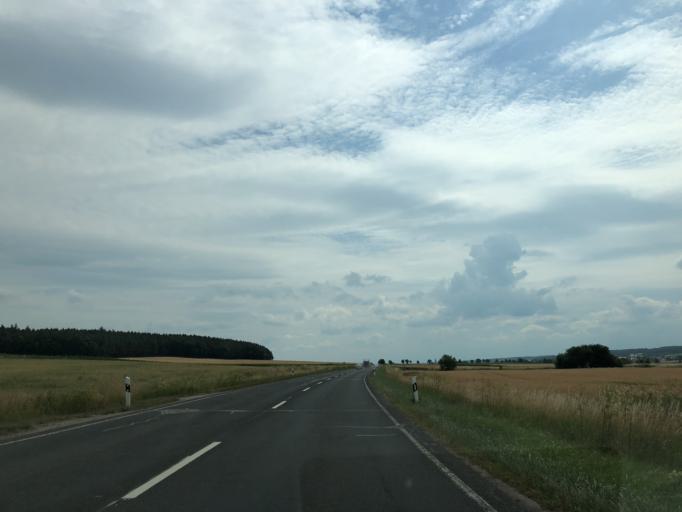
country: DE
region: Bavaria
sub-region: Regierungsbezirk Mittelfranken
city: Wachenroth
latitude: 49.7517
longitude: 10.7257
